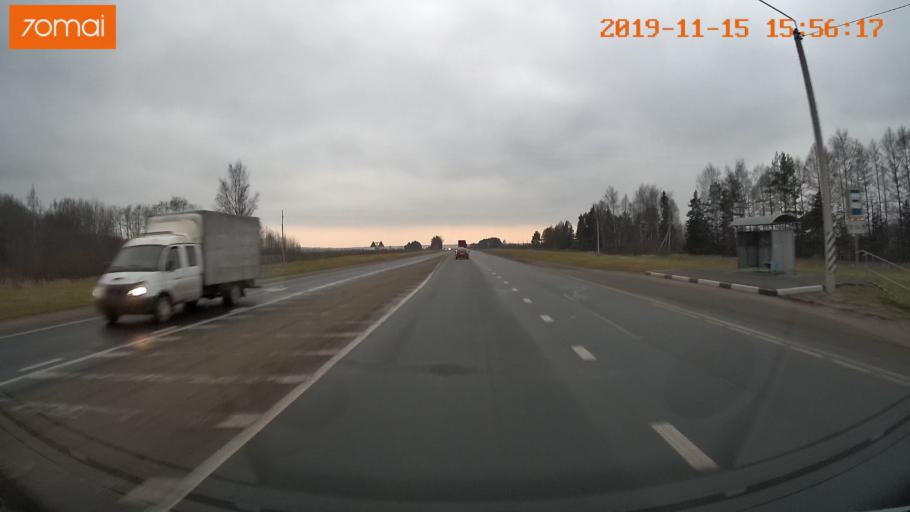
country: RU
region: Jaroslavl
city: Yaroslavl
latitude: 57.8439
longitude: 39.9752
